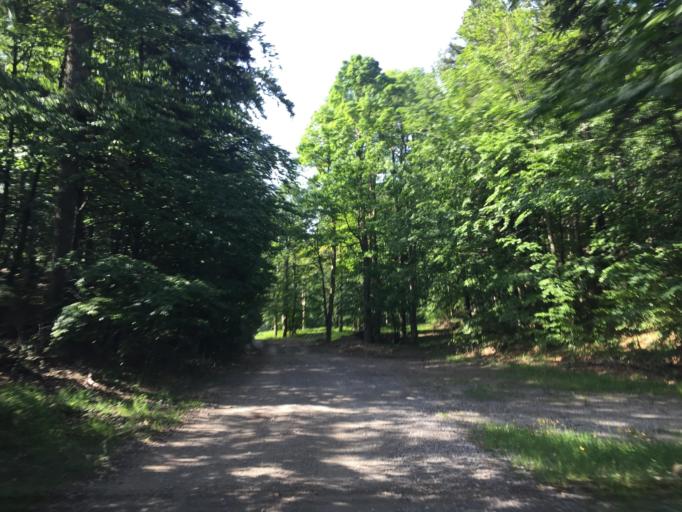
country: HR
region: Primorsko-Goranska
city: Podhum
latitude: 45.4472
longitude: 14.5550
